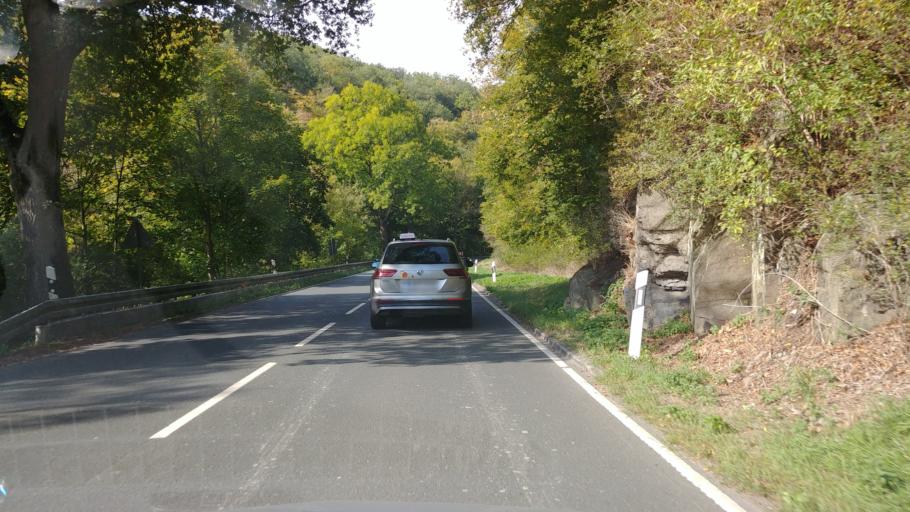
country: DE
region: Hesse
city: Burg Hohenstein
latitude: 50.1792
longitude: 8.0686
